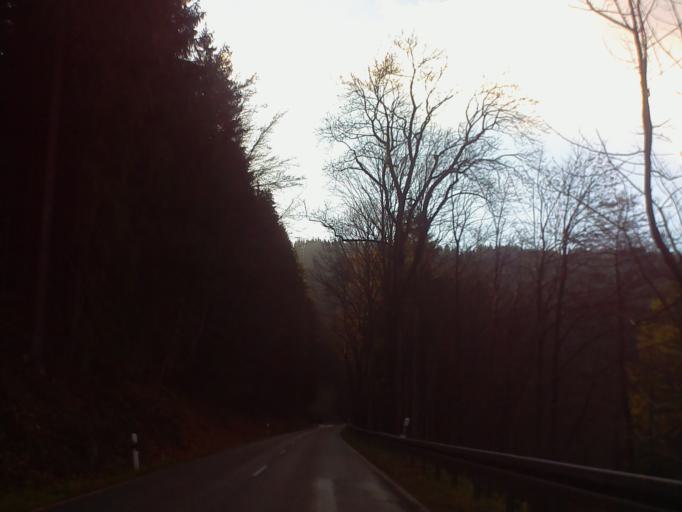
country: DE
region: Thuringia
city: Katzhutte
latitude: 50.5670
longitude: 11.0710
